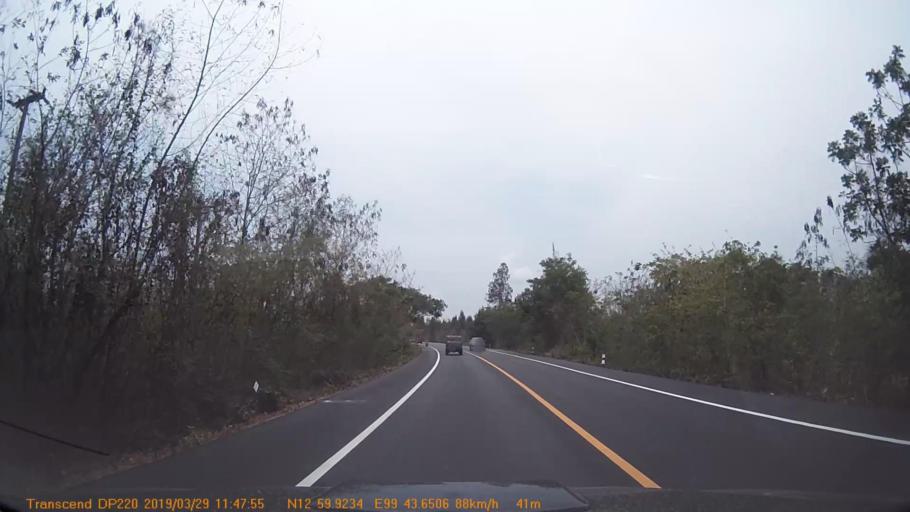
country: TH
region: Phetchaburi
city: Kaeng Krachan
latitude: 12.9983
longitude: 99.7277
